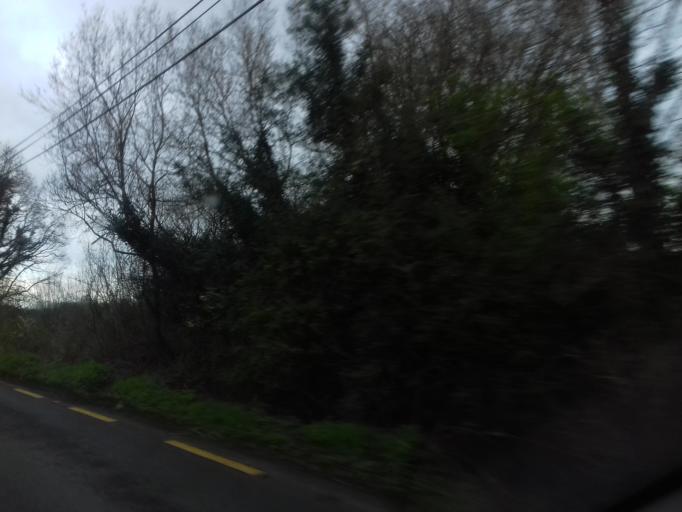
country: IE
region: Ulster
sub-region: An Cabhan
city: Ballyconnell
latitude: 54.1459
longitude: -7.7058
